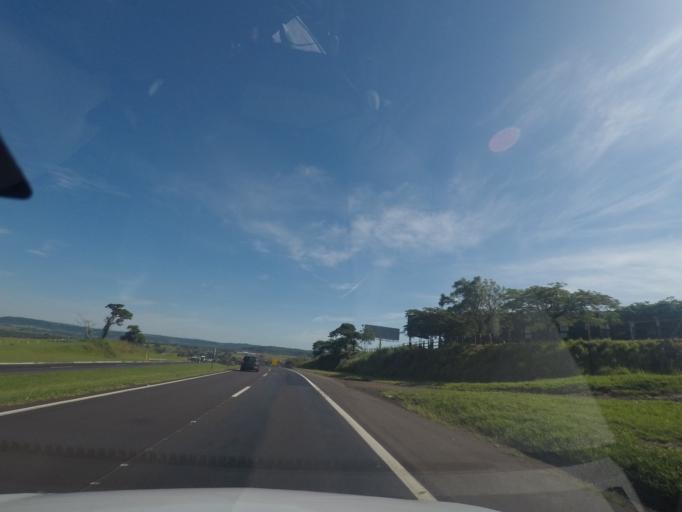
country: BR
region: Sao Paulo
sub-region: Rio Claro
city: Rio Claro
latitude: -22.3381
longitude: -47.6510
